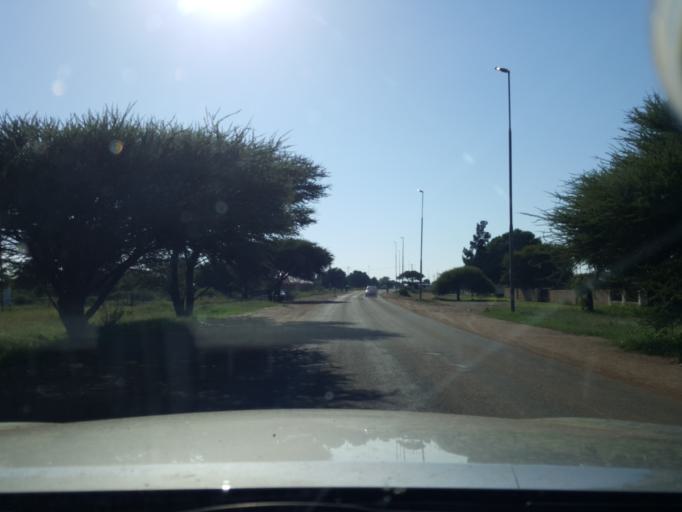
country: ZA
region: North-West
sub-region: Ngaka Modiri Molema District Municipality
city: Mmabatho
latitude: -25.8258
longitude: 25.6423
